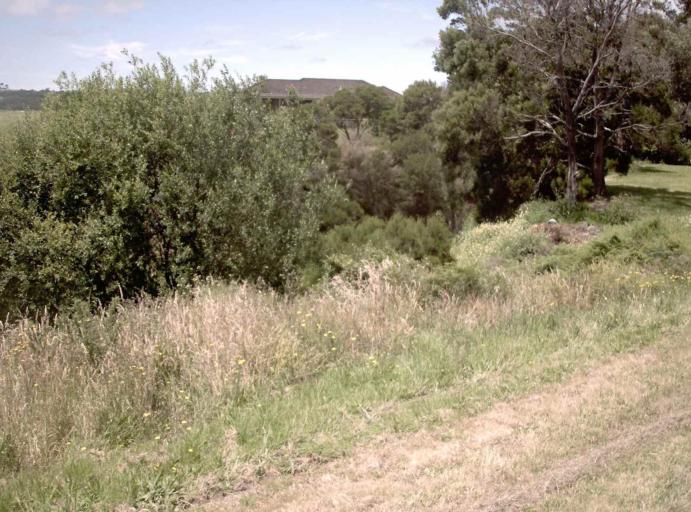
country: AU
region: Victoria
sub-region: Bass Coast
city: North Wonthaggi
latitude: -38.7096
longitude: 146.0895
